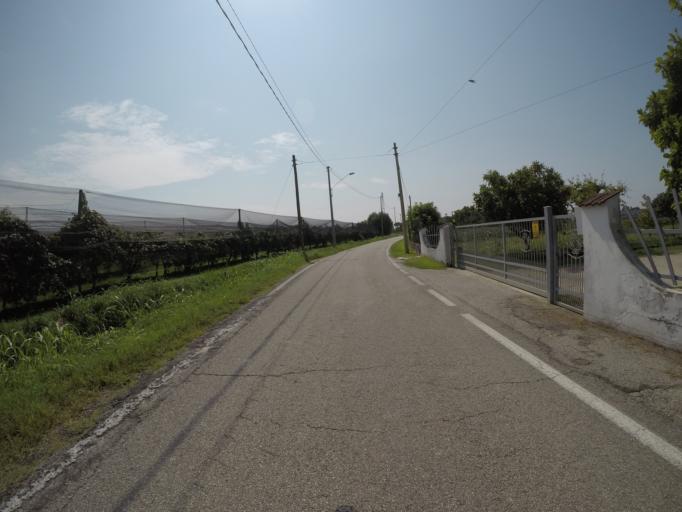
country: IT
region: Veneto
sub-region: Provincia di Rovigo
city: Lendinara
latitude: 45.0916
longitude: 11.5897
